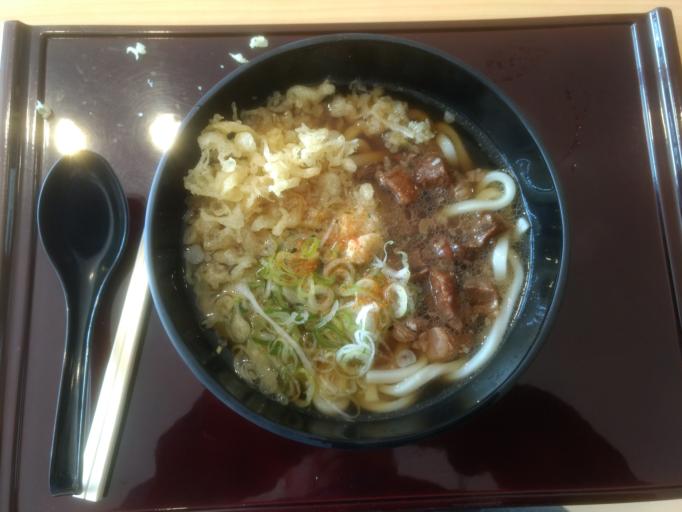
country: JP
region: Kumamoto
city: Yatsushiro
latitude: 32.5438
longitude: 130.6805
